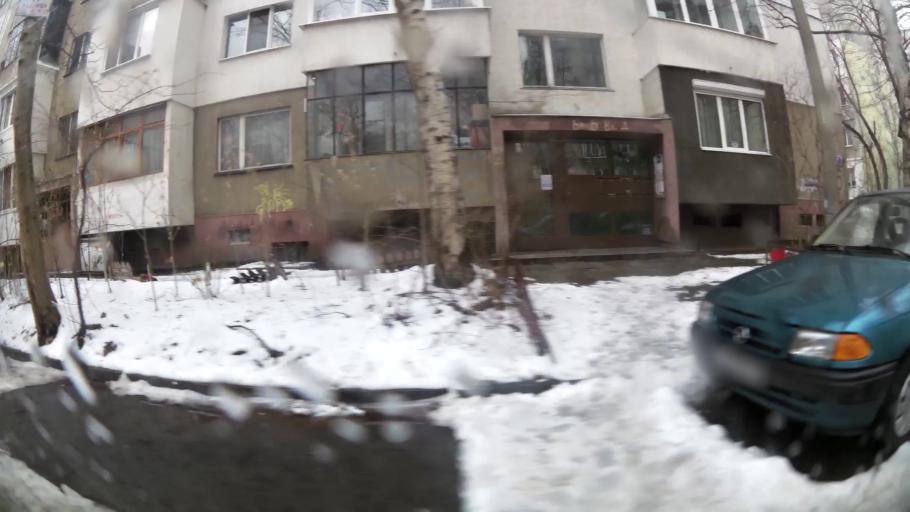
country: BG
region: Sofia-Capital
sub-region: Stolichna Obshtina
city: Sofia
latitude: 42.6707
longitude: 23.2758
